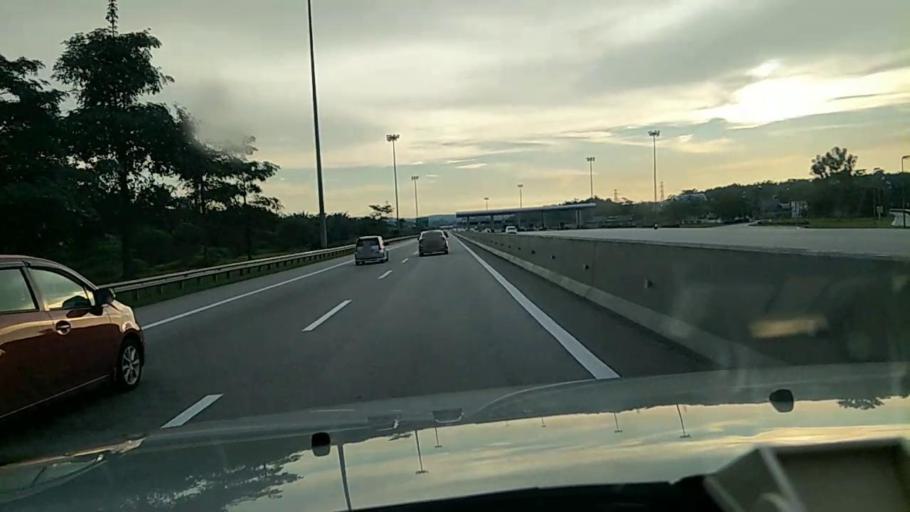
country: MY
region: Selangor
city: Ladang Seri Kundang
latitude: 3.2709
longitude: 101.5334
